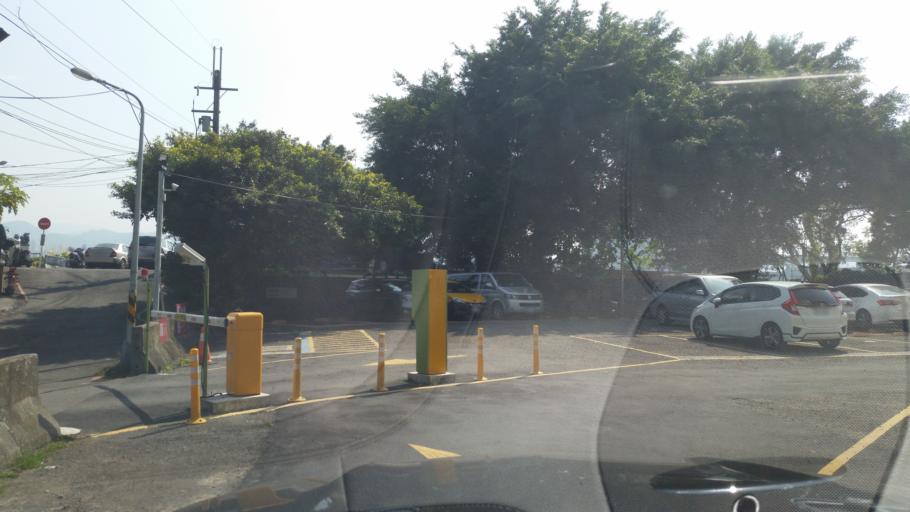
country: TW
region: Taipei
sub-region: Taipei
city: Banqiao
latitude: 24.9862
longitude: 121.5221
